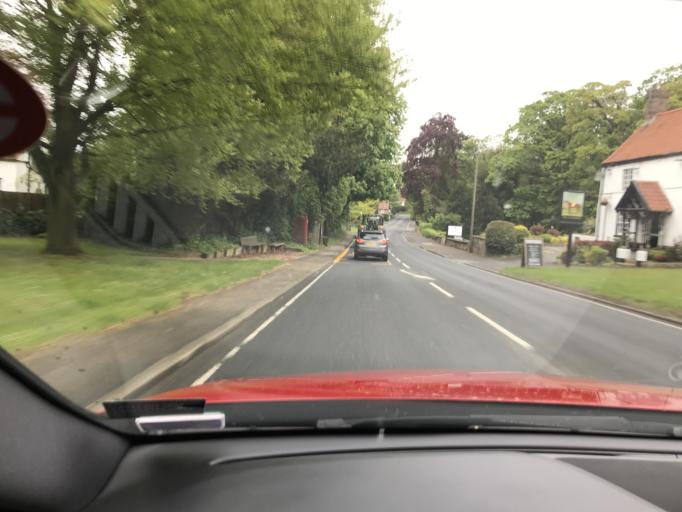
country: GB
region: England
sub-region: East Riding of Yorkshire
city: Cherry Burton
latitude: 53.8456
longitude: -0.4981
